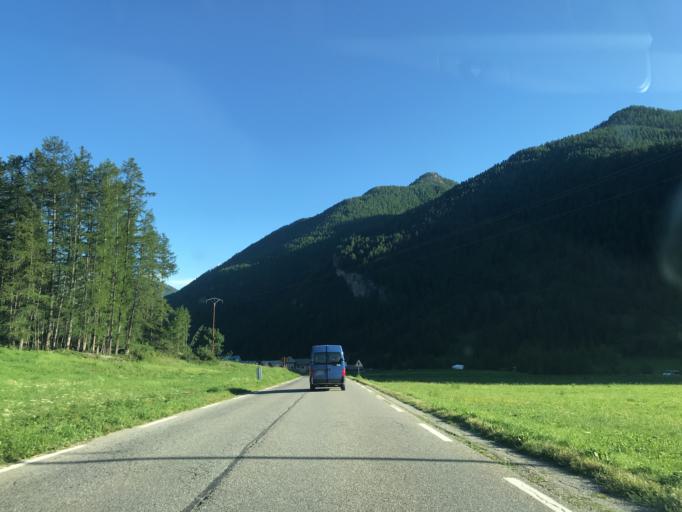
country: FR
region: Provence-Alpes-Cote d'Azur
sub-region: Departement des Hautes-Alpes
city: Guillestre
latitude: 44.7721
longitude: 6.7365
